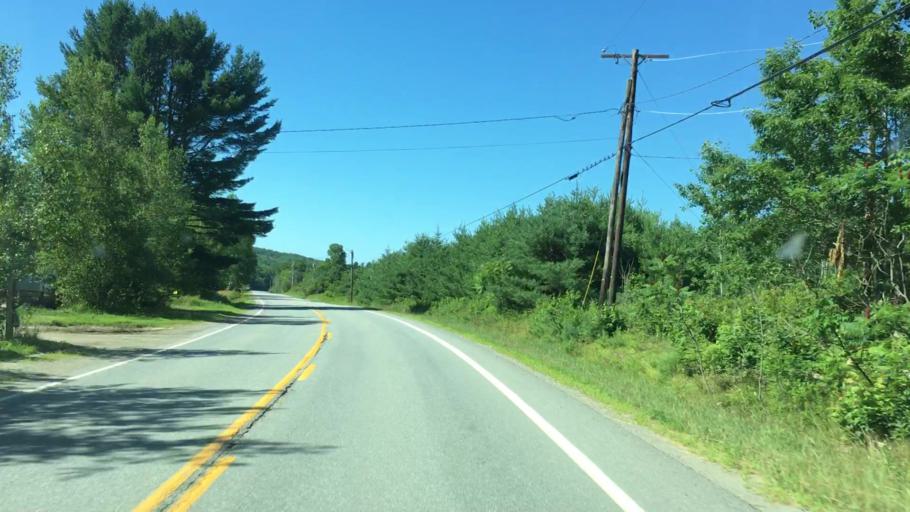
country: US
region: Maine
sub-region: Hancock County
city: Dedham
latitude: 44.6741
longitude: -68.6718
